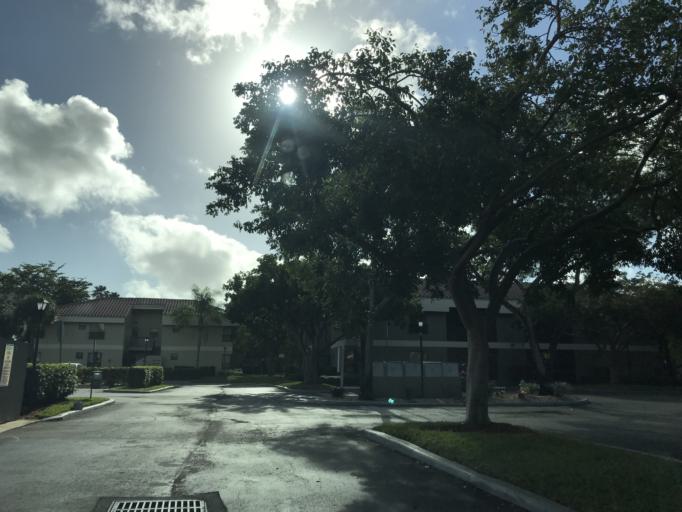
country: US
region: Florida
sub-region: Broward County
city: Coconut Creek
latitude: 26.2607
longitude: -80.1919
